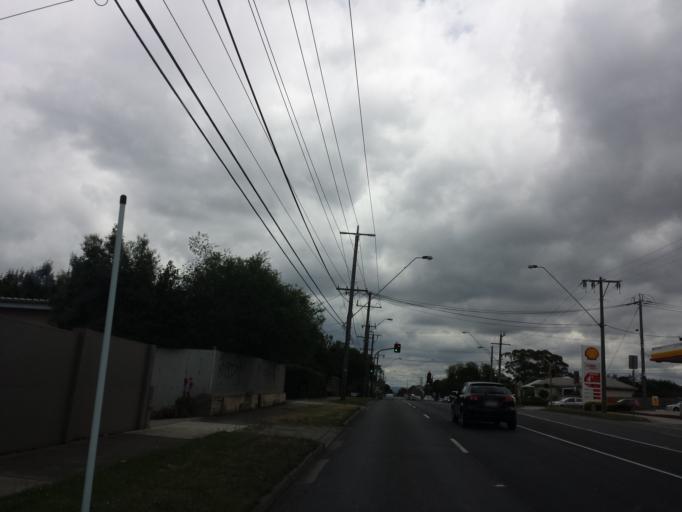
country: AU
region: Victoria
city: Watsonia
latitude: -37.7201
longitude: 145.0810
